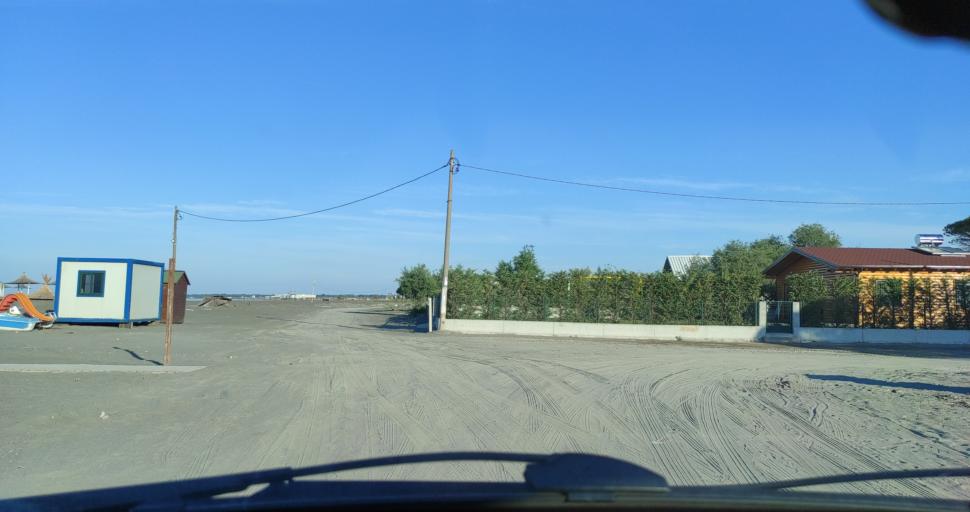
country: AL
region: Shkoder
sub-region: Rrethi i Shkodres
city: Velipoje
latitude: 41.8602
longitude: 19.4375
